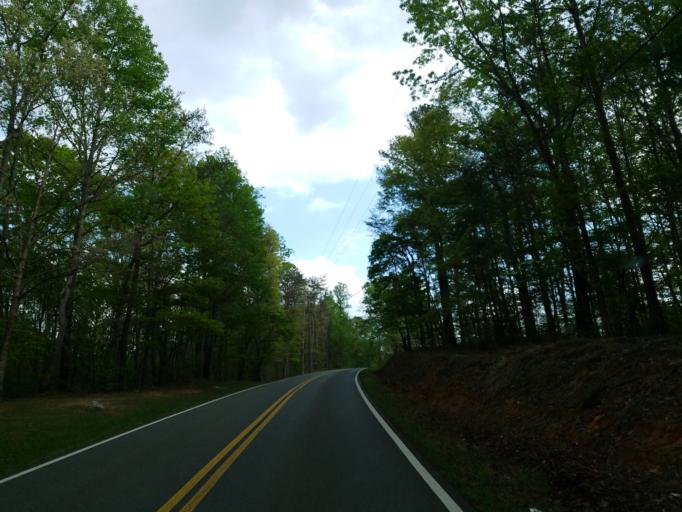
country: US
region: Georgia
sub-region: Pickens County
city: Jasper
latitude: 34.4382
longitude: -84.4673
